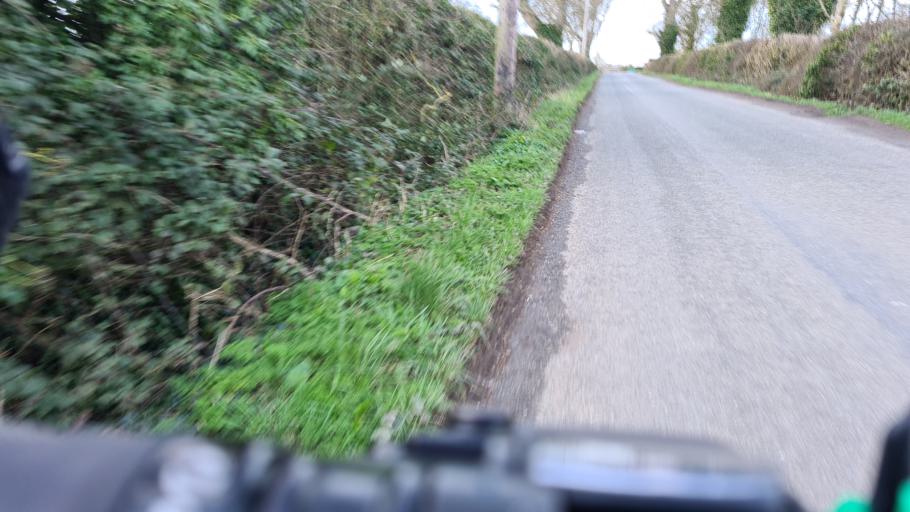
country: IE
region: Leinster
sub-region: Kildare
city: Celbridge
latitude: 53.3483
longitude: -6.5758
